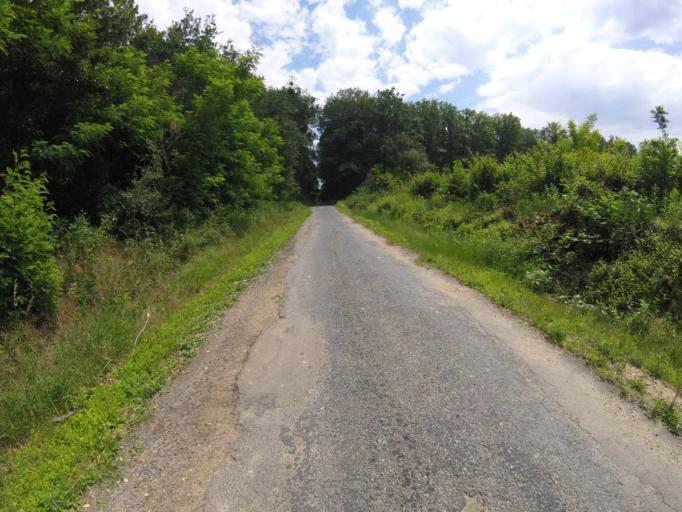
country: HU
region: Zala
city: Turje
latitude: 47.0432
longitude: 17.0354
